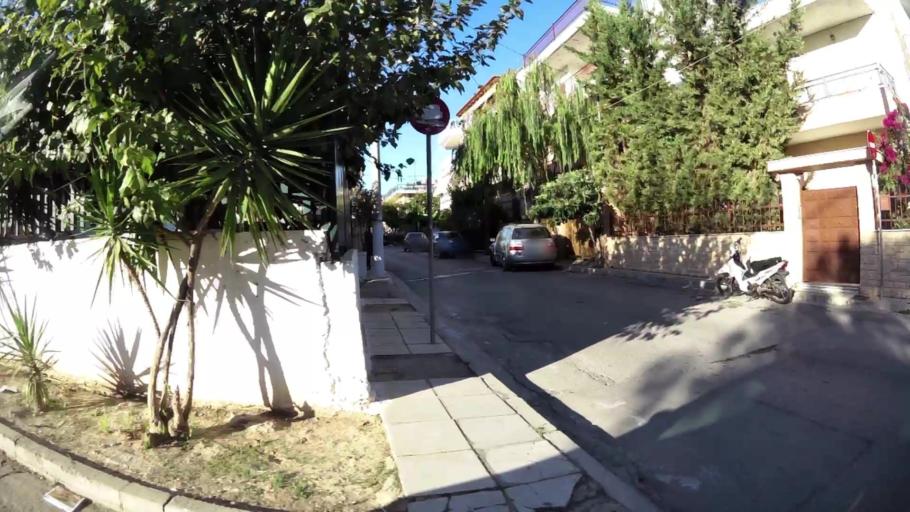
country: GR
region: Attica
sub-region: Nomarchia Anatolikis Attikis
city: Acharnes
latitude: 38.0805
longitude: 23.7283
